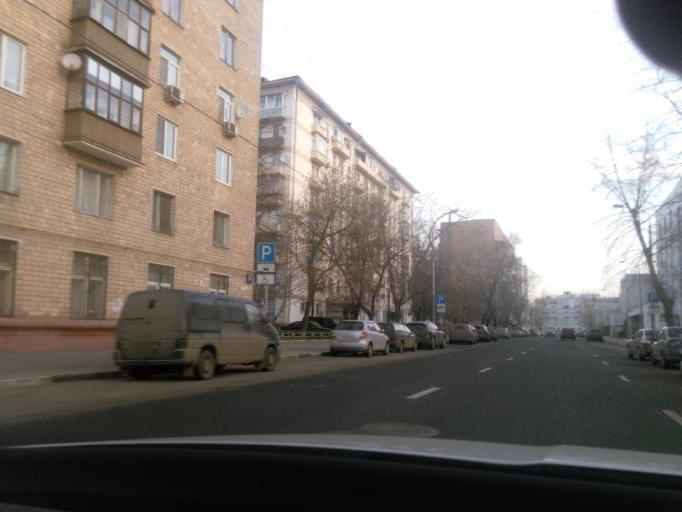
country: RU
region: Moscow
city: Zamoskvorech'ye
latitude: 55.7188
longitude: 37.6256
